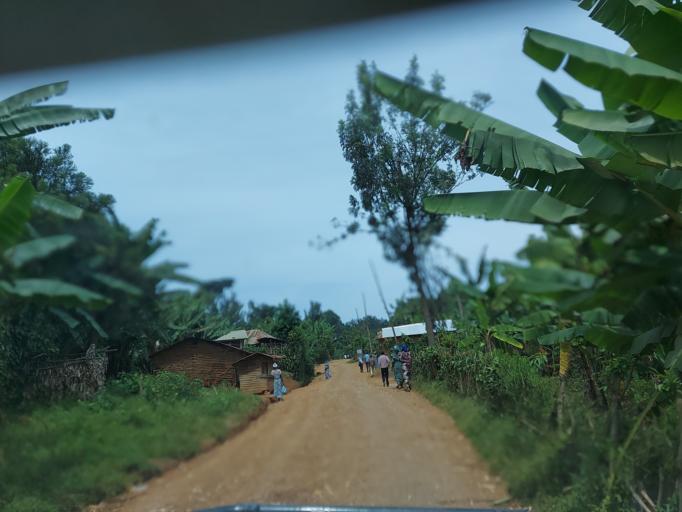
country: CD
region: South Kivu
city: Bukavu
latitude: -2.2344
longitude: 28.8508
